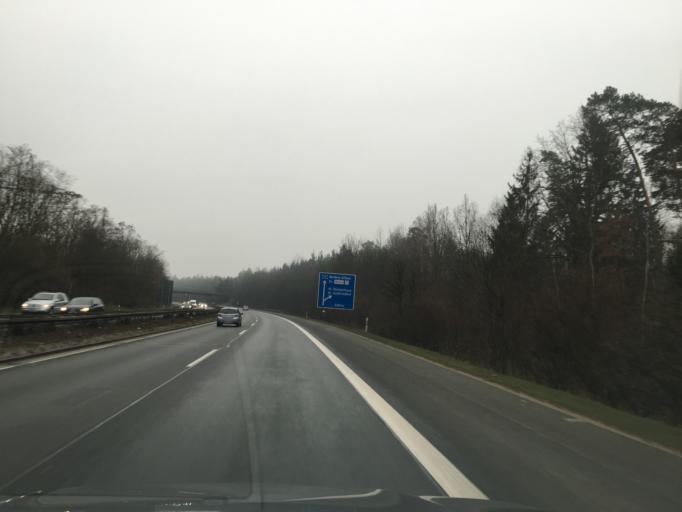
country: DE
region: Bavaria
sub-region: Regierungsbezirk Mittelfranken
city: Nuernberg
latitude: 49.4012
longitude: 11.0739
